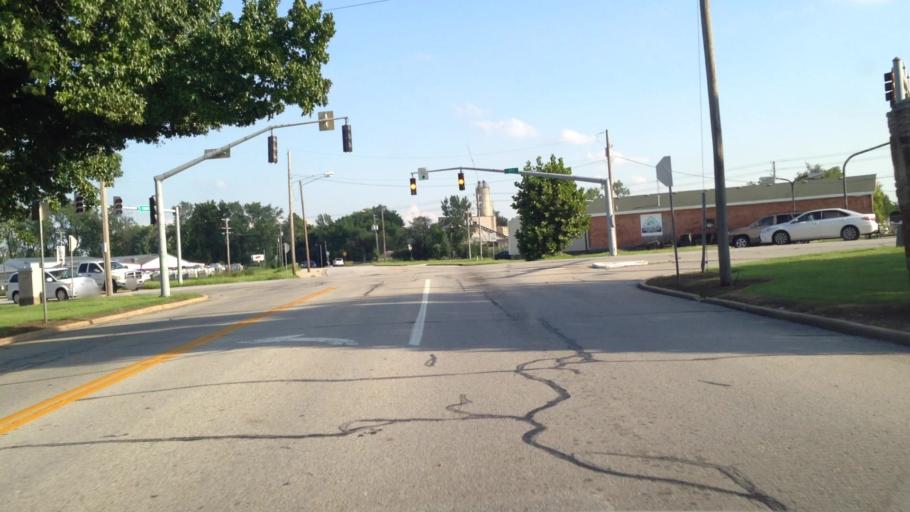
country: US
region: Missouri
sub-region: Jasper County
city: Joplin
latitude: 37.0879
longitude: -94.5072
